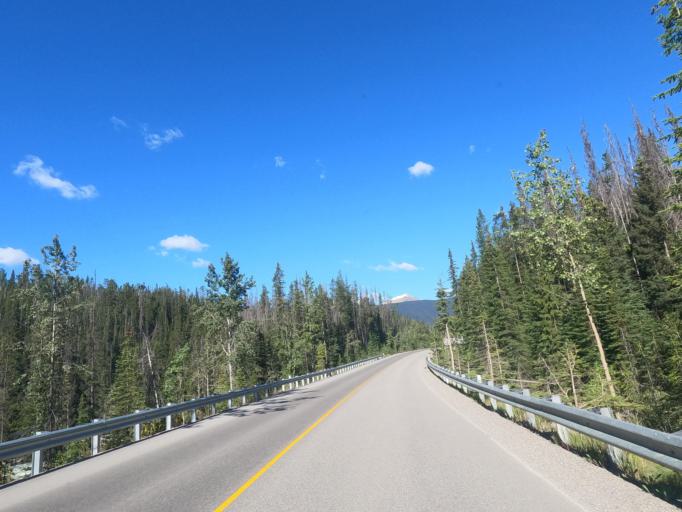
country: CA
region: Alberta
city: Lake Louise
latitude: 51.3799
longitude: -116.5150
